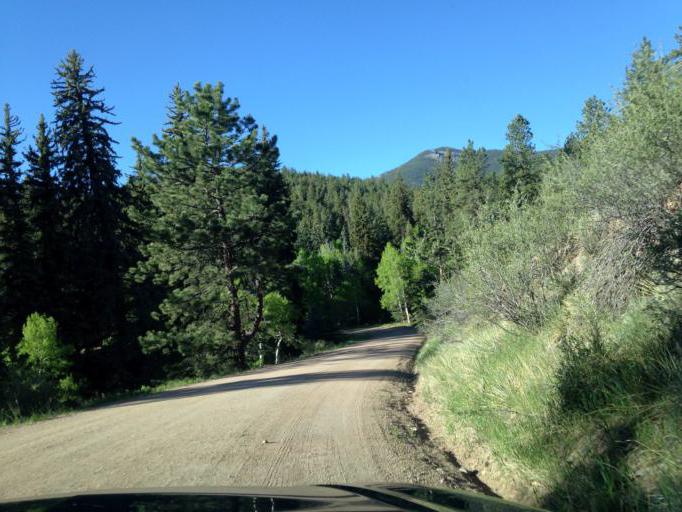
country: US
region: Colorado
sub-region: Jefferson County
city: Evergreen
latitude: 39.4094
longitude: -105.5258
